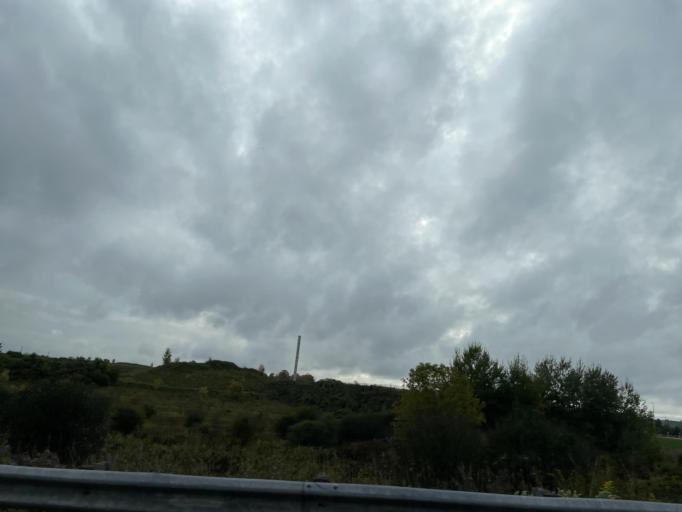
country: CA
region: Ontario
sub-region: Wellington County
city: Guelph
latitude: 43.5548
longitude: -80.1919
